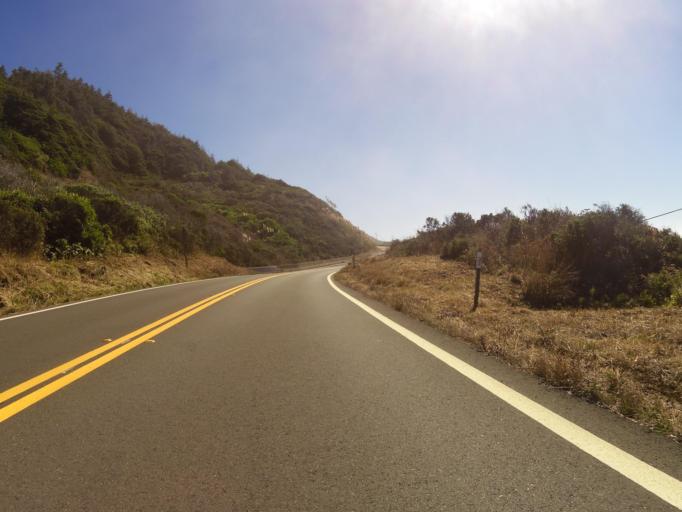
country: US
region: California
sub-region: Mendocino County
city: Fort Bragg
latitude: 39.6121
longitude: -123.7822
